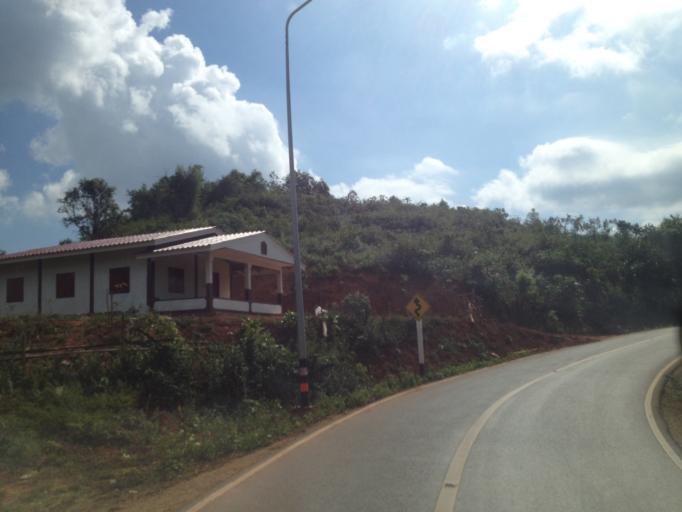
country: TH
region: Mae Hong Son
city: Ban Huai I Huak
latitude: 18.1487
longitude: 98.1355
